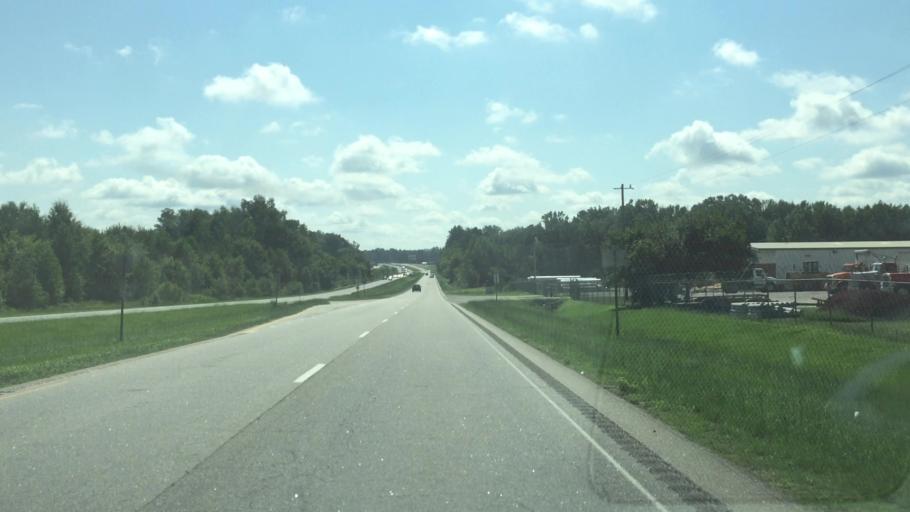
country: US
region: North Carolina
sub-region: Anson County
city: Wadesboro
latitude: 34.9815
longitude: -80.1308
